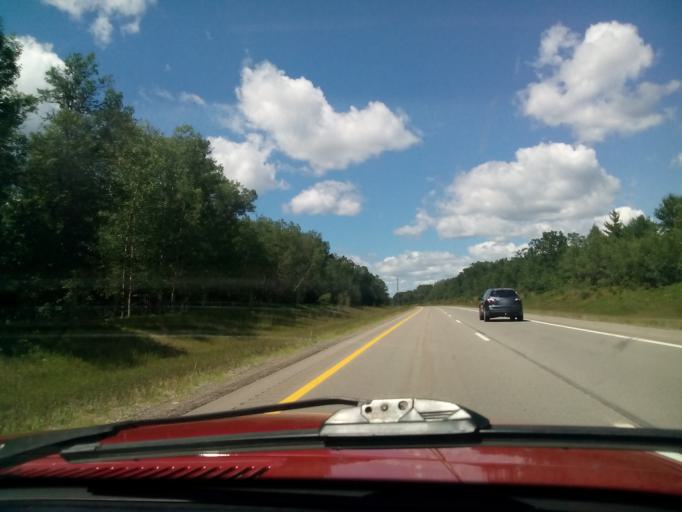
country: US
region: Michigan
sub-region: Roscommon County
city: Roscommon
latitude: 44.4690
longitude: -84.6149
